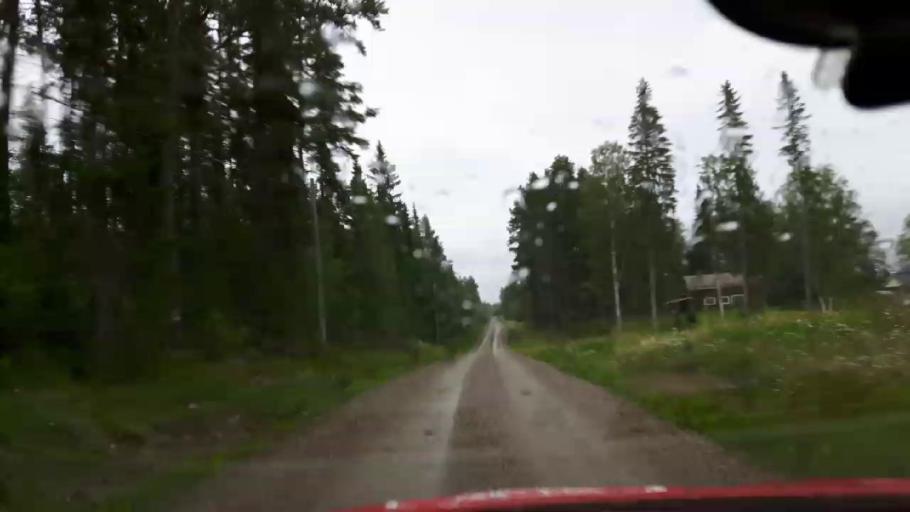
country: SE
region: Jaemtland
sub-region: OEstersunds Kommun
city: Brunflo
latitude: 62.8158
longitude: 14.9213
